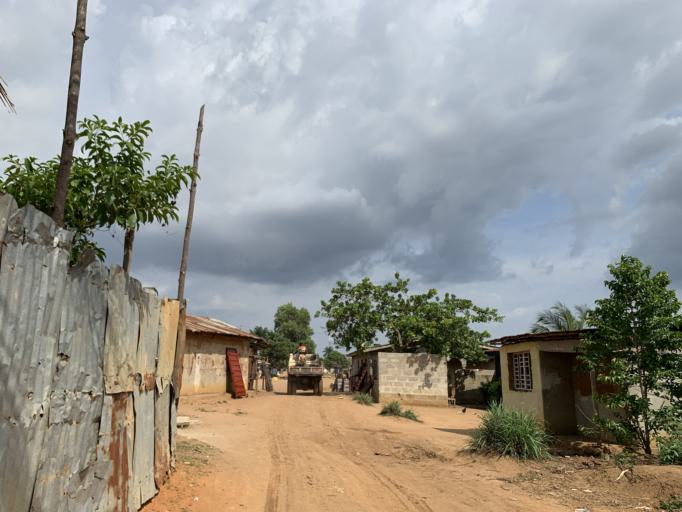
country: SL
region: Western Area
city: Waterloo
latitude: 8.3494
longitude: -13.0425
